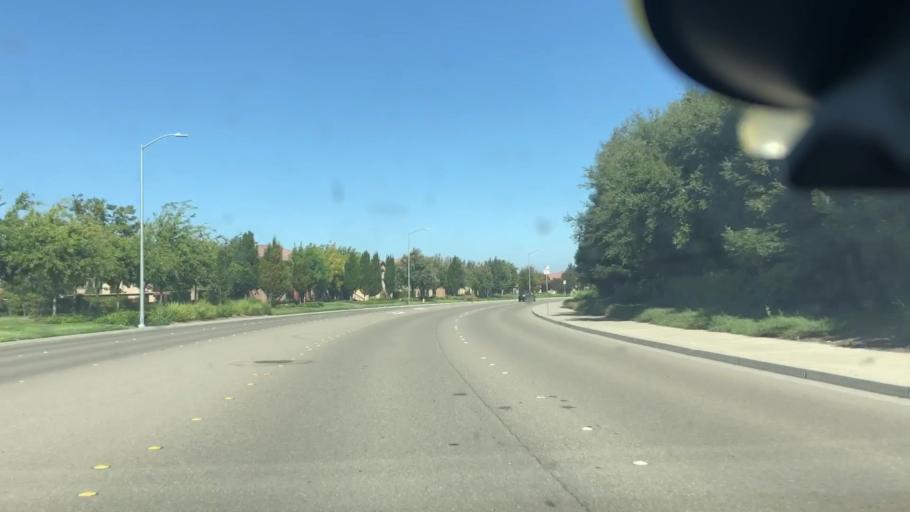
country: US
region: California
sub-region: San Joaquin County
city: Manteca
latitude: 37.7814
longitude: -121.2057
